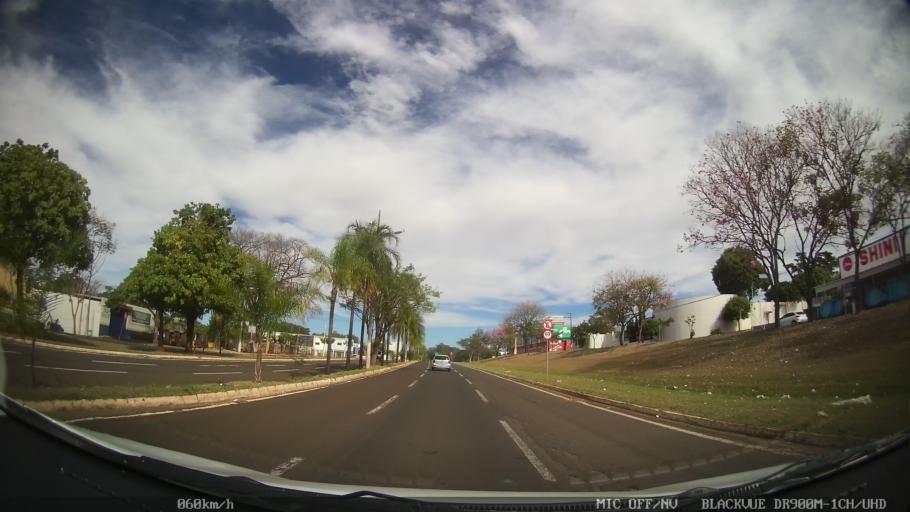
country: BR
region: Sao Paulo
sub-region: Catanduva
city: Catanduva
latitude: -21.1533
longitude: -48.9819
